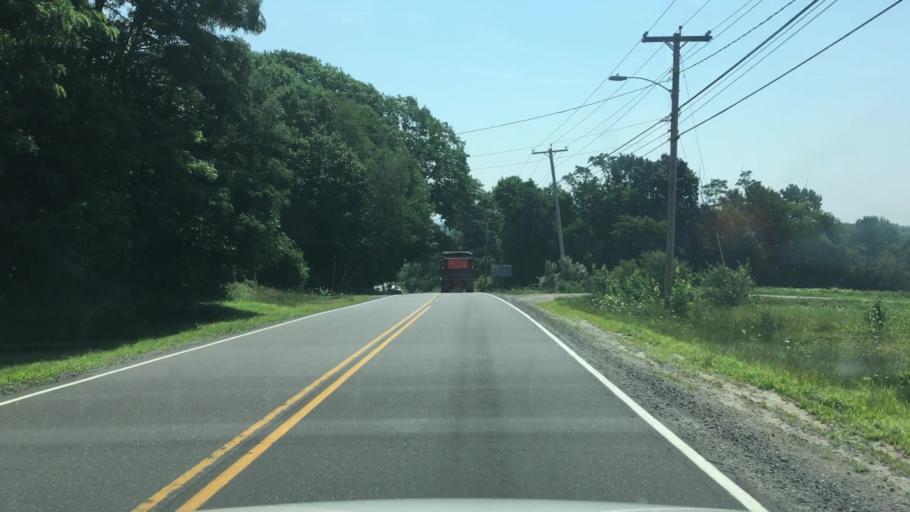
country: US
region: Maine
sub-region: Kennebec County
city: Hallowell
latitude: 44.3040
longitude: -69.8196
